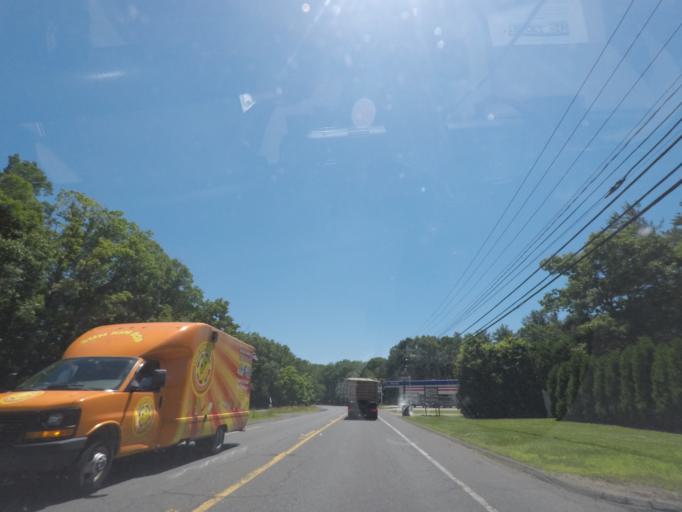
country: US
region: Massachusetts
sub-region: Hampden County
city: Westfield
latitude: 42.1507
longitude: -72.8143
